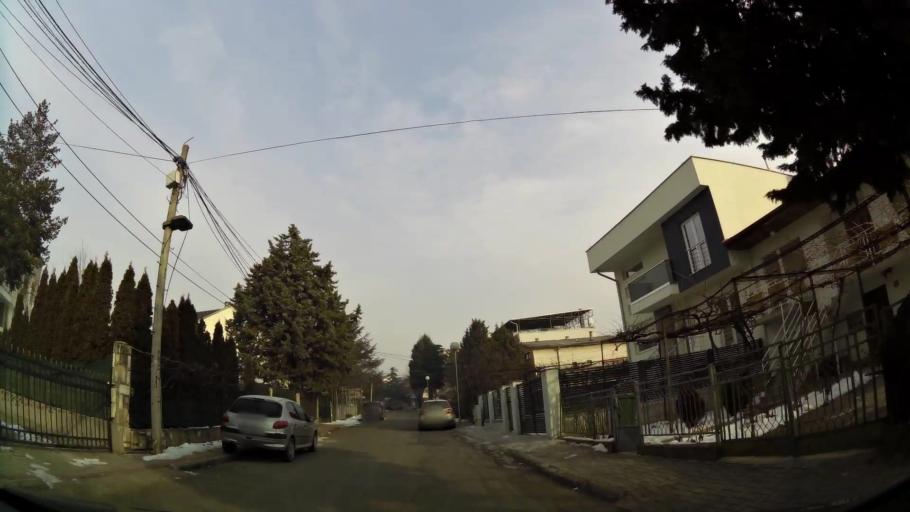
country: MK
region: Butel
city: Butel
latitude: 42.0202
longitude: 21.4532
